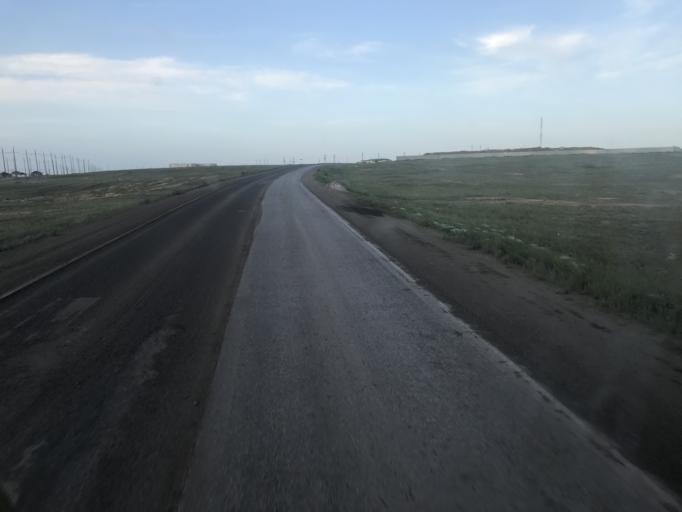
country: KZ
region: Aqtoebe
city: Khromtau
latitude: 50.2587
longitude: 58.3979
